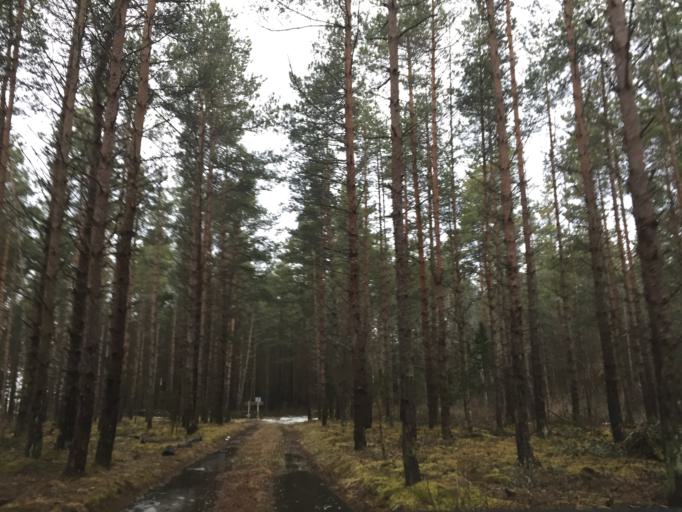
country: EE
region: Saare
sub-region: Orissaare vald
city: Orissaare
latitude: 58.6123
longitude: 22.9562
